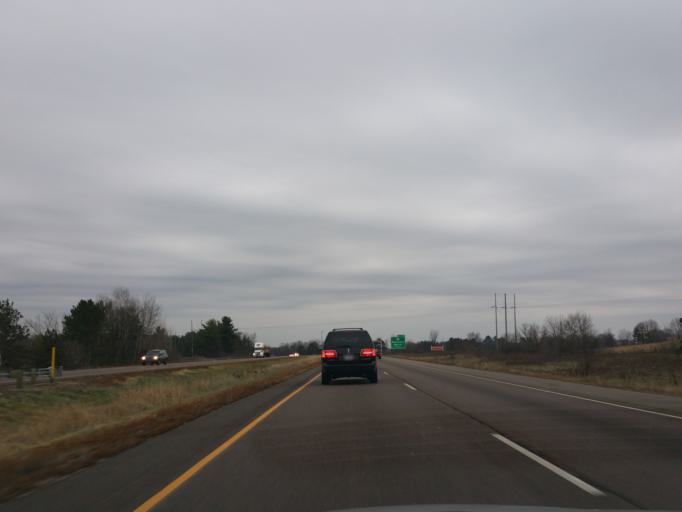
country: US
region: Wisconsin
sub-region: Dunn County
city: Menomonie
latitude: 44.9092
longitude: -91.9647
